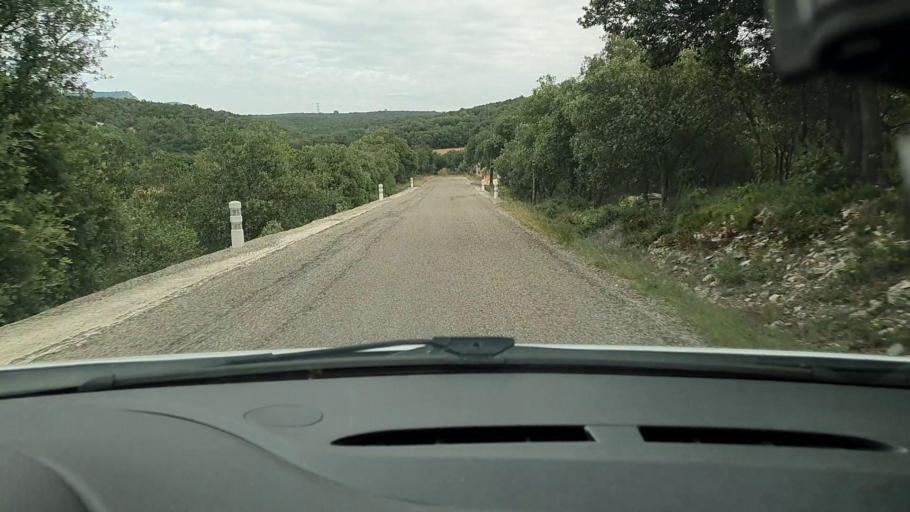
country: FR
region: Languedoc-Roussillon
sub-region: Departement du Gard
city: Montaren-et-Saint-Mediers
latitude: 44.0731
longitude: 4.3133
